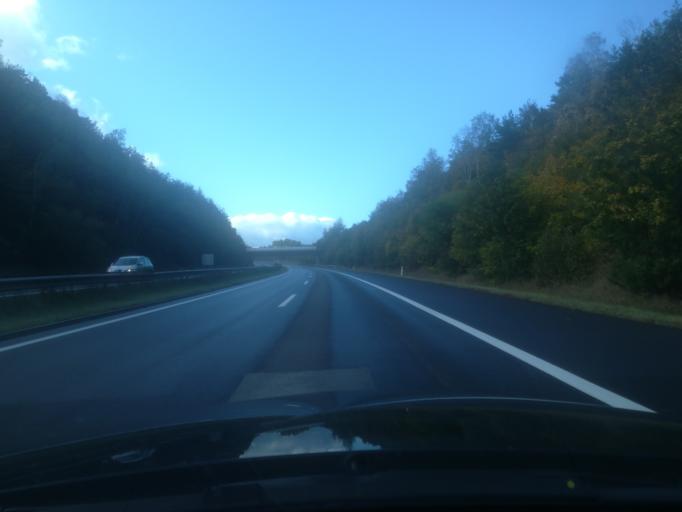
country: AT
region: Upper Austria
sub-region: Politischer Bezirk Urfahr-Umgebung
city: Gallneukirchen
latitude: 48.3382
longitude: 14.4139
